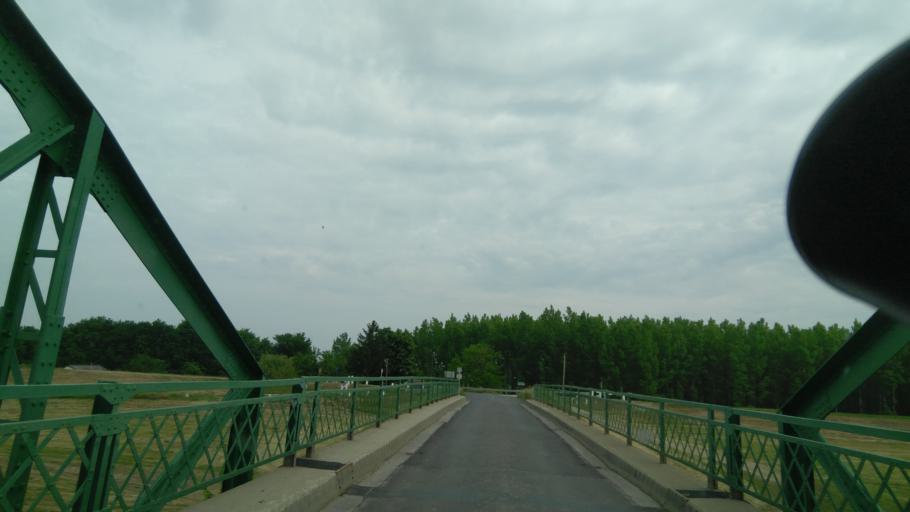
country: HU
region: Bekes
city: Szeghalom
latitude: 46.9877
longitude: 21.1827
